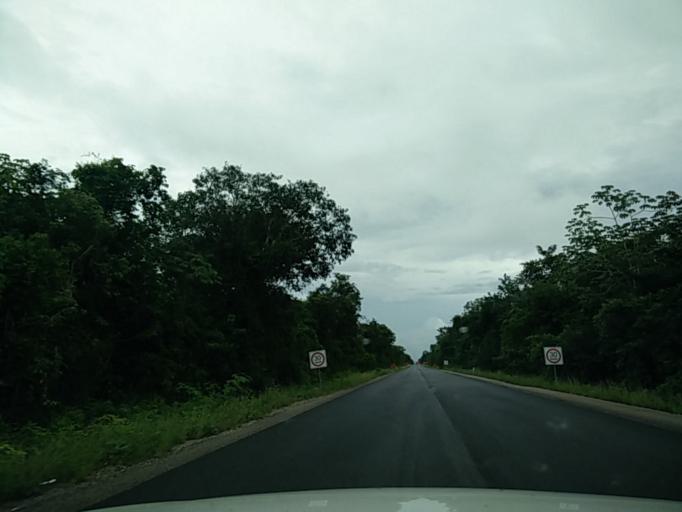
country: MX
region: Quintana Roo
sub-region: Lazaro Cardenas
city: El Tintal
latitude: 20.8963
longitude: -87.4927
